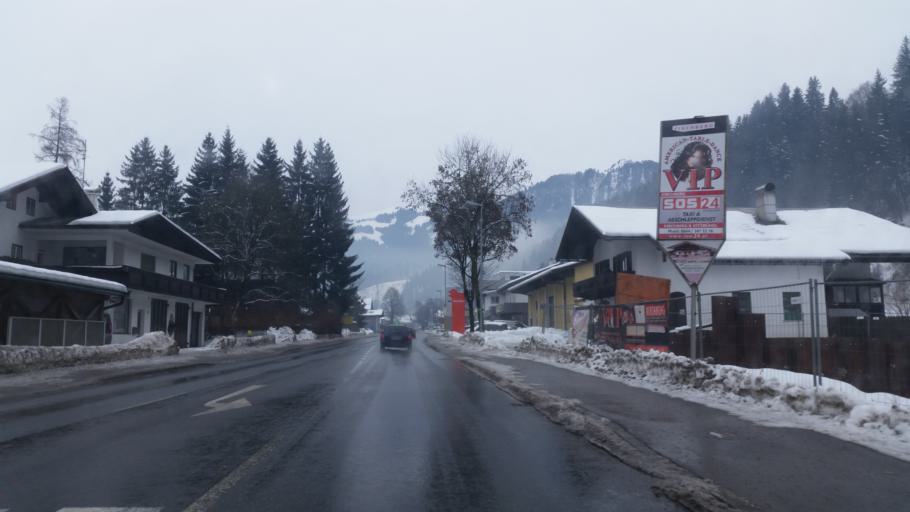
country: AT
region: Tyrol
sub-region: Politischer Bezirk Kitzbuhel
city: Kitzbuhel
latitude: 47.4615
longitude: 12.3862
